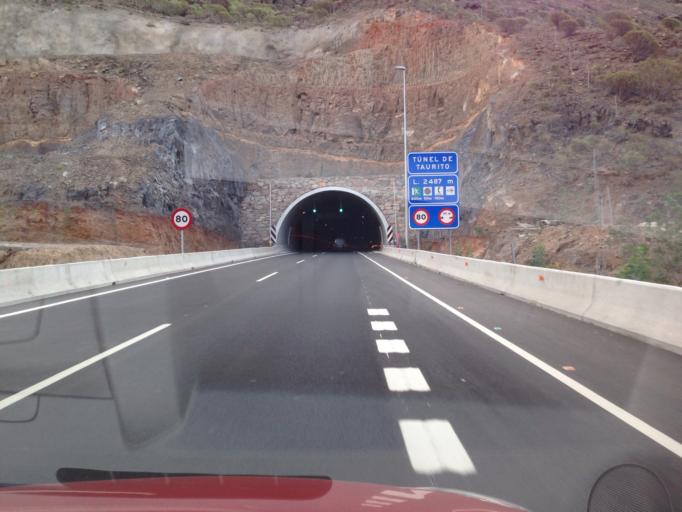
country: ES
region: Canary Islands
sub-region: Provincia de Las Palmas
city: Puerto Rico
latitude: 27.8253
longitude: -15.7462
